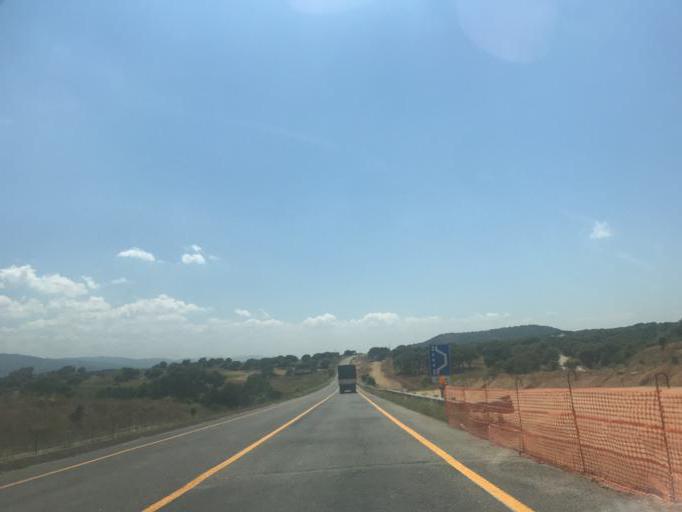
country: IT
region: Sardinia
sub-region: Provincia di Olbia-Tempio
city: Monti
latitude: 40.7853
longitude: 9.2530
